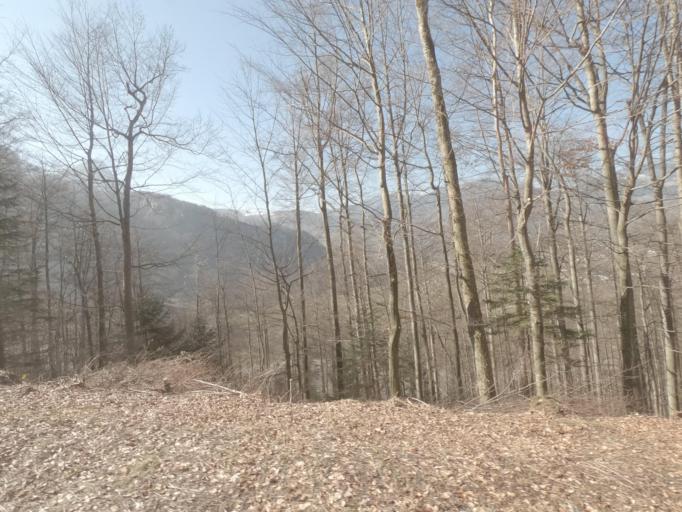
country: CH
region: Obwalden
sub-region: Obwalden
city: Giswil
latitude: 46.8225
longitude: 8.1835
